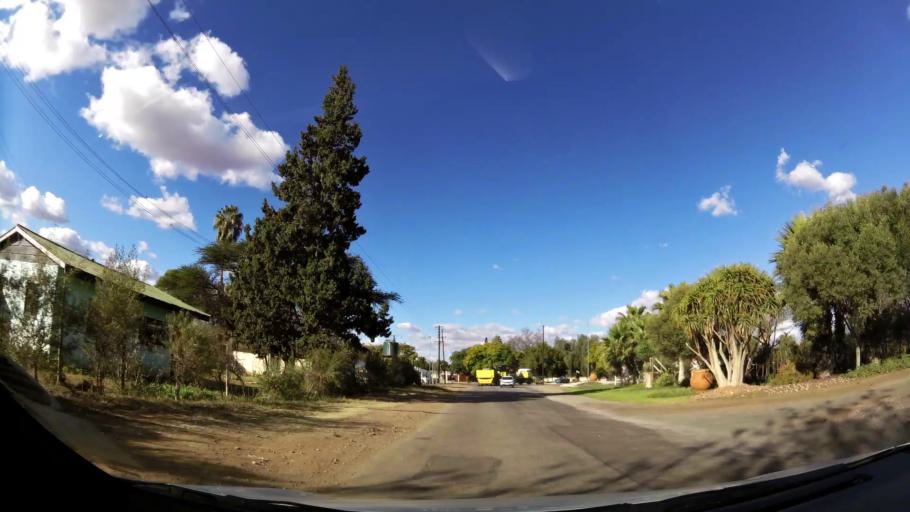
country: ZA
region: Limpopo
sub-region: Capricorn District Municipality
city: Polokwane
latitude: -23.9298
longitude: 29.4498
